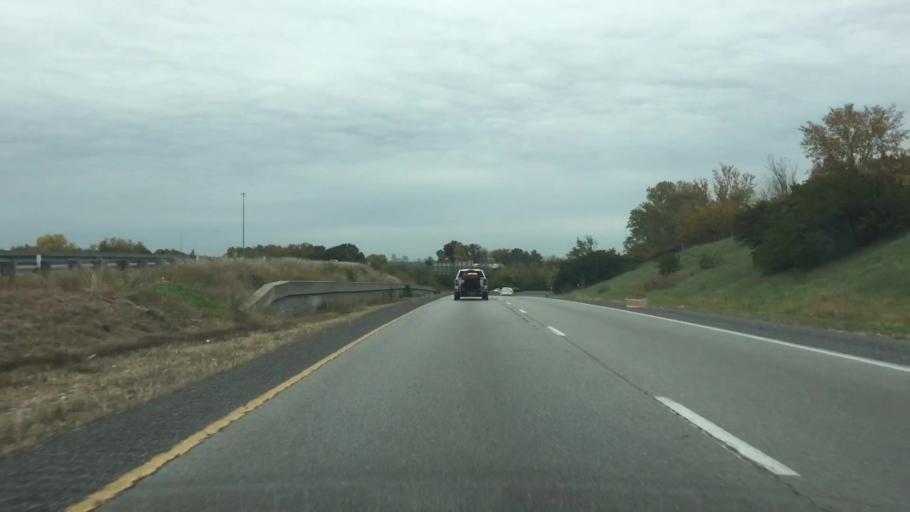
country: US
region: Missouri
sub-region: Jackson County
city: Raytown
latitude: 39.0199
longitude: -94.4991
